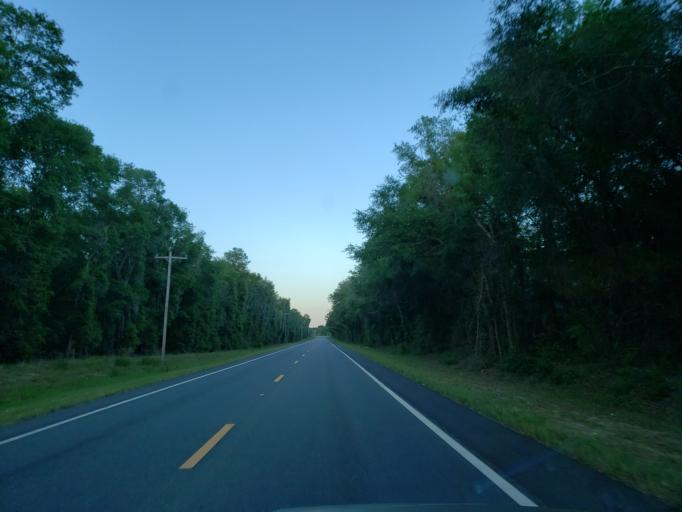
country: US
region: Georgia
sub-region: Echols County
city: Statenville
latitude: 30.5814
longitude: -83.1800
